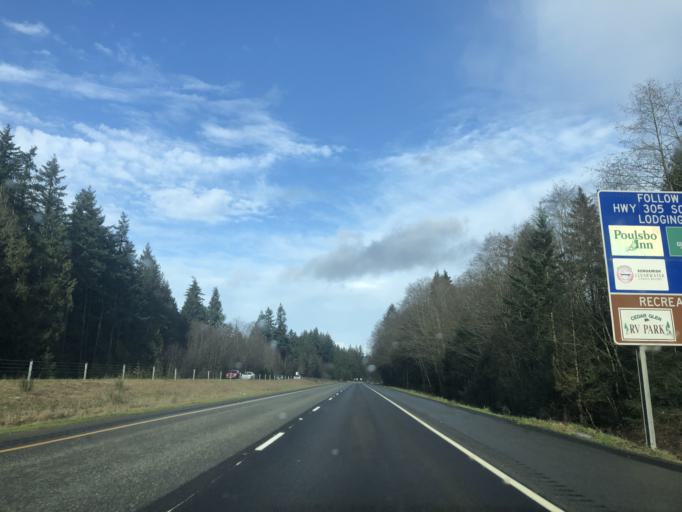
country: US
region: Washington
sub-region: Kitsap County
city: Poulsbo
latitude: 47.7443
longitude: -122.6716
